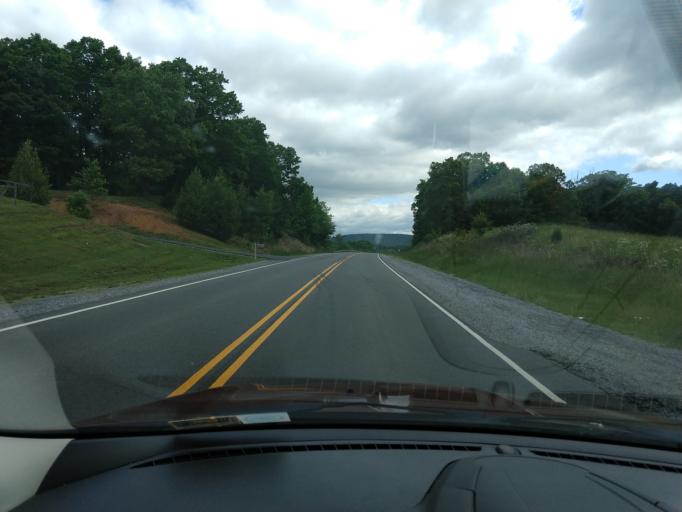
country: US
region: Virginia
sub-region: Wythe County
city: Wytheville
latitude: 36.8793
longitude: -80.9815
